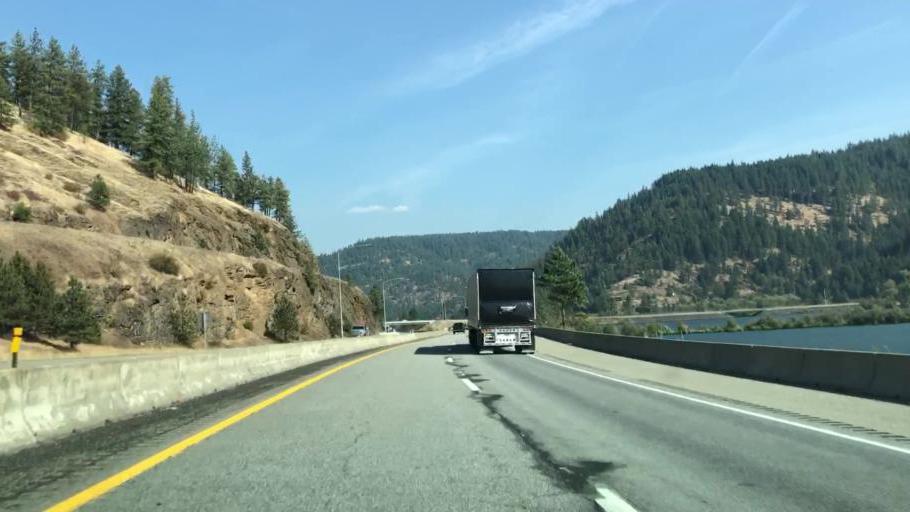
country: US
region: Idaho
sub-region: Kootenai County
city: Coeur d'Alene
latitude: 47.6230
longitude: -116.6572
